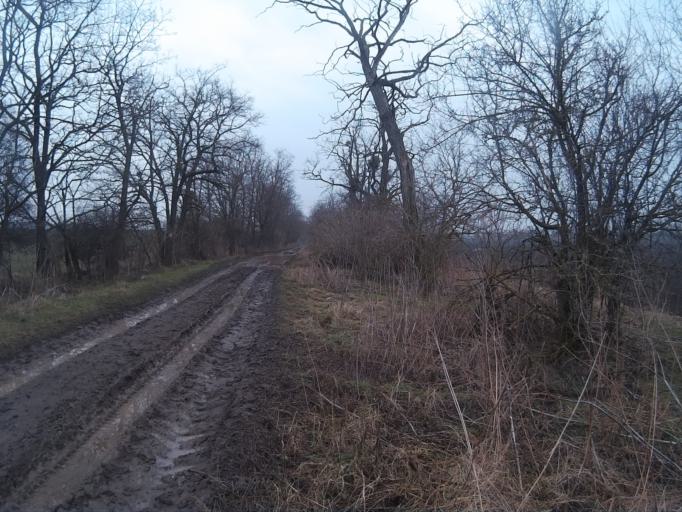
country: HU
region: Fejer
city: Szarliget
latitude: 47.5504
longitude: 18.5632
